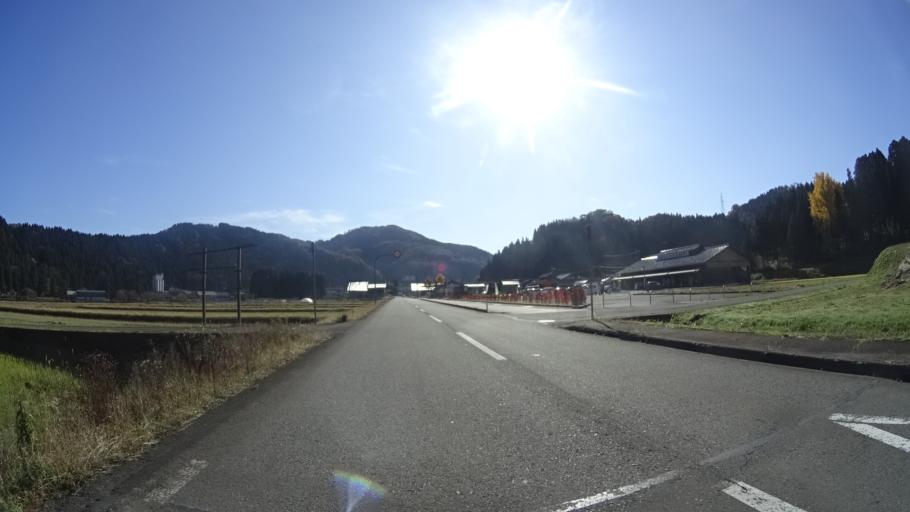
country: JP
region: Ishikawa
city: Tsurugi-asahimachi
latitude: 36.3614
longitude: 136.5988
